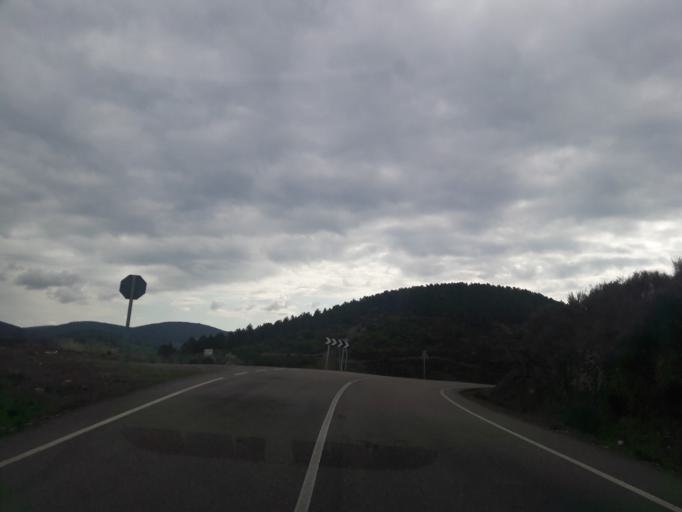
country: ES
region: Castille and Leon
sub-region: Provincia de Salamanca
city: Serradilla del Arroyo
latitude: 40.5152
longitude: -6.3915
